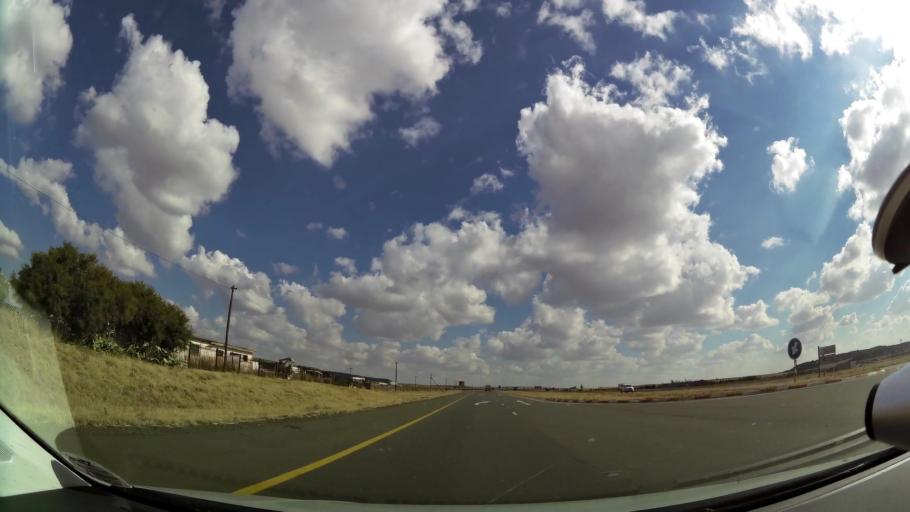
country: ZA
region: Orange Free State
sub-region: Mangaung Metropolitan Municipality
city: Bloemfontein
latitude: -29.1437
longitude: 26.0912
